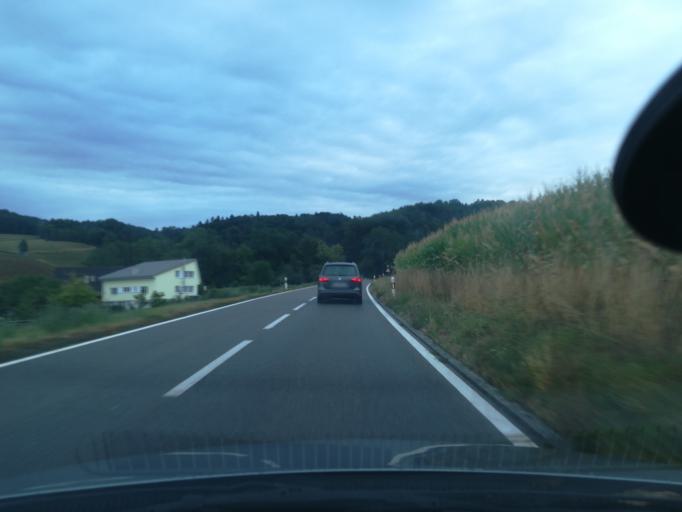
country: CH
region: Thurgau
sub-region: Frauenfeld District
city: Eschenz
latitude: 47.6421
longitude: 8.8756
